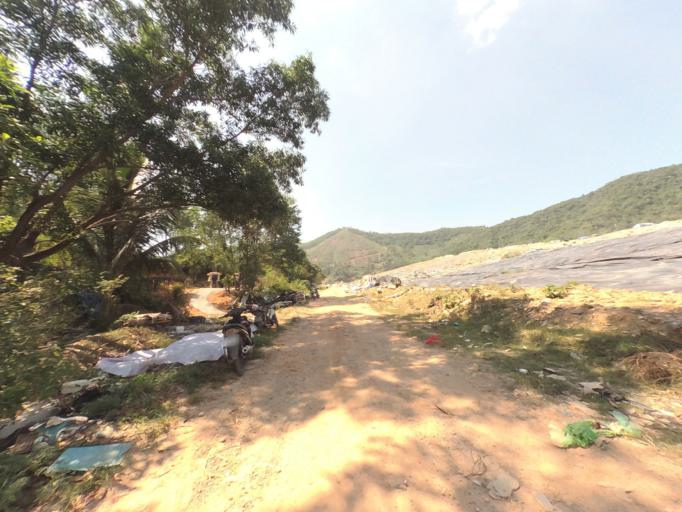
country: VN
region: Da Nang
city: Lien Chieu
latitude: 16.0428
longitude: 108.1429
